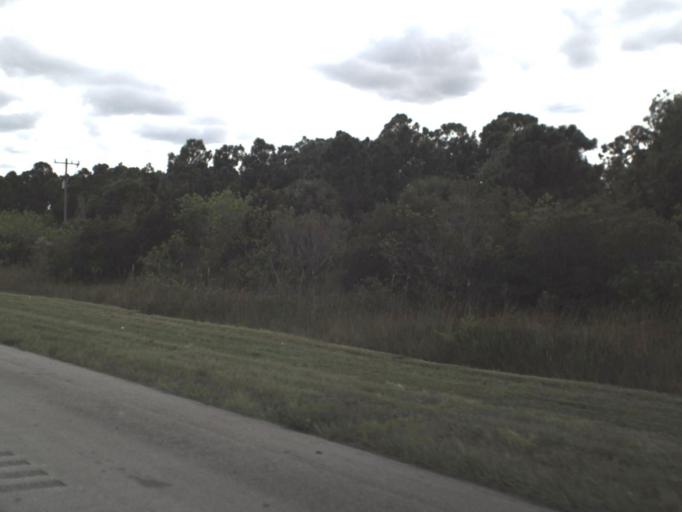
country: US
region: Florida
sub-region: Saint Lucie County
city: White City
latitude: 27.3618
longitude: -80.3778
